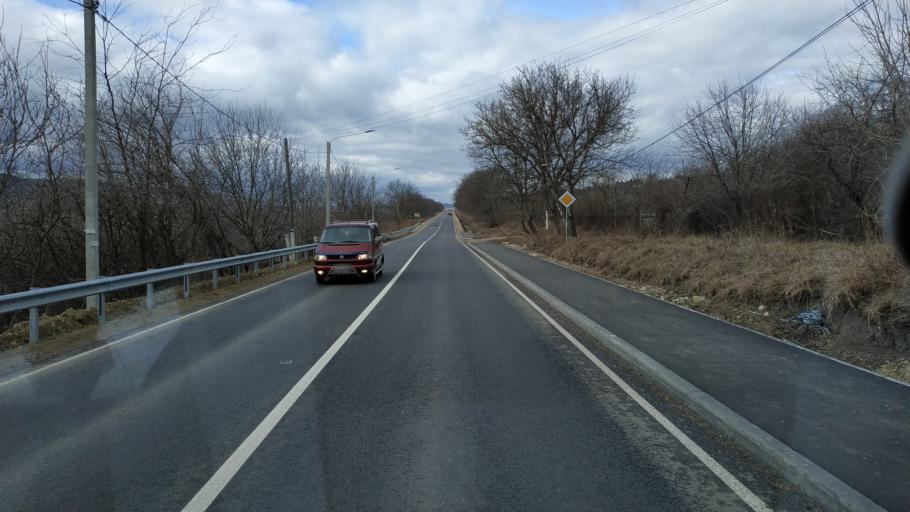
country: MD
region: Stinga Nistrului
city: Bucovat
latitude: 47.2031
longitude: 28.4280
